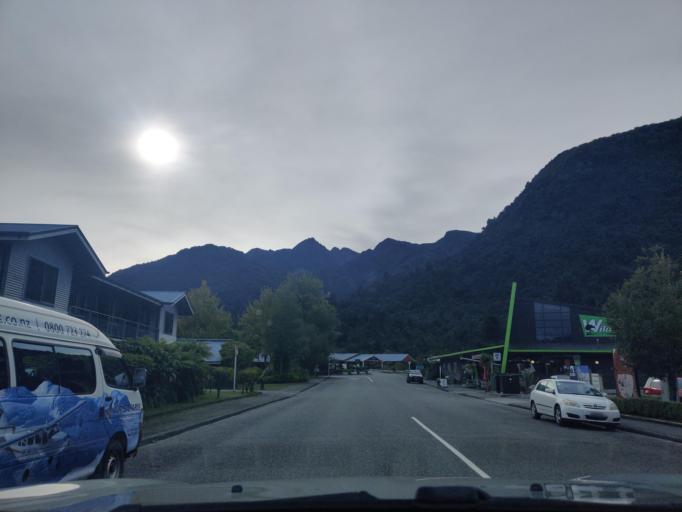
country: NZ
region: West Coast
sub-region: Westland District
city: Hokitika
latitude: -43.3872
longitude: 170.1821
